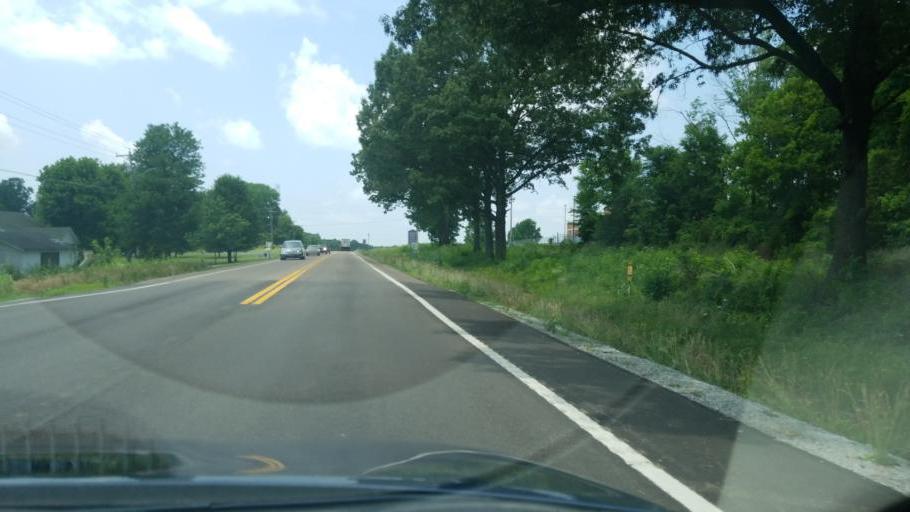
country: US
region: Tennessee
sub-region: Carroll County
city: Huntingdon
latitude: 36.0196
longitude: -88.3745
